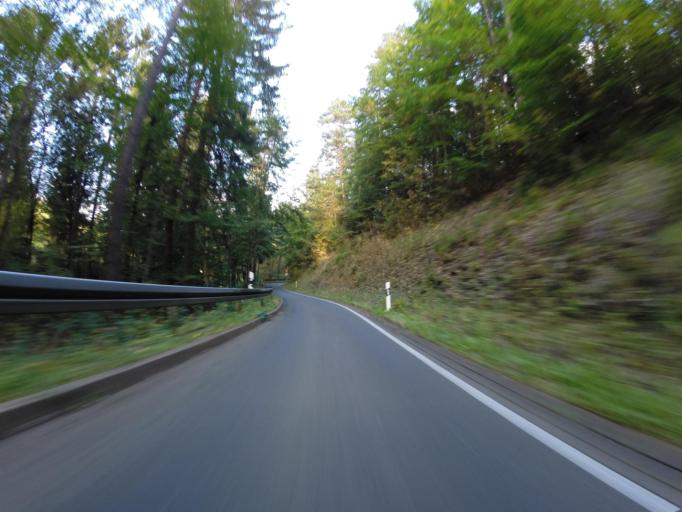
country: DE
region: Thuringia
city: Bucha
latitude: 50.9256
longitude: 11.5306
